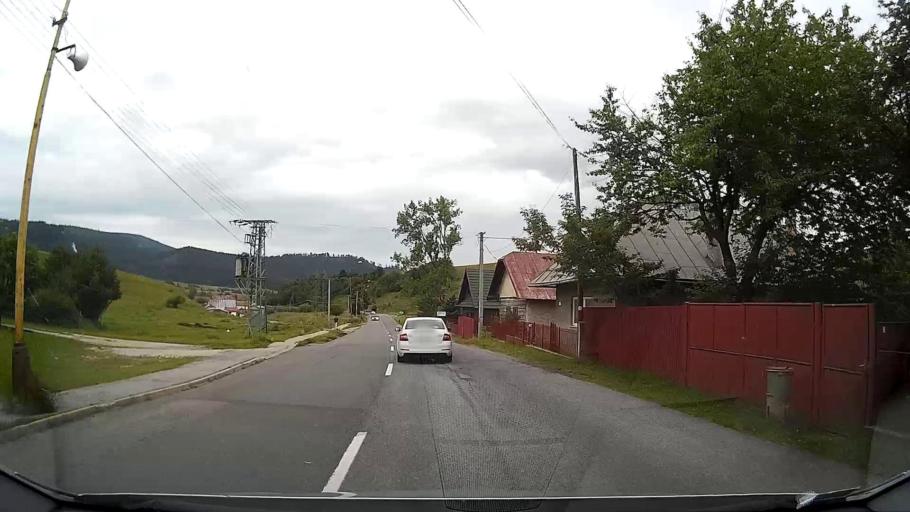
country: SK
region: Banskobystricky
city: Revuca
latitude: 48.8465
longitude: 20.1832
